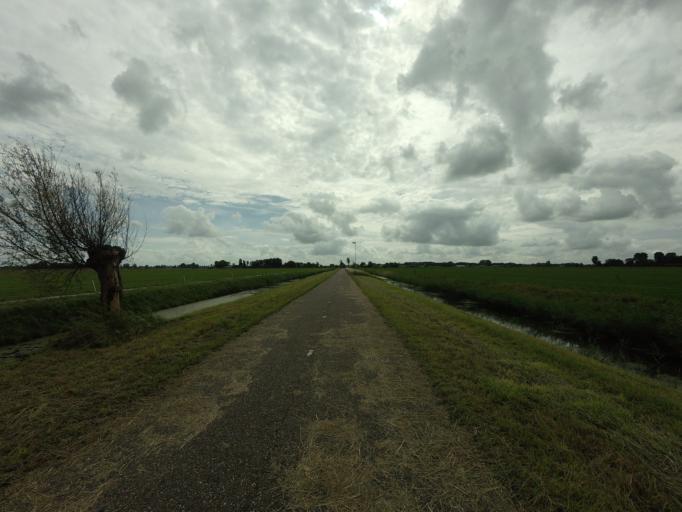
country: NL
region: North Holland
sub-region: Gemeente Medemblik
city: Opperdoes
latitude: 52.7058
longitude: 5.0696
